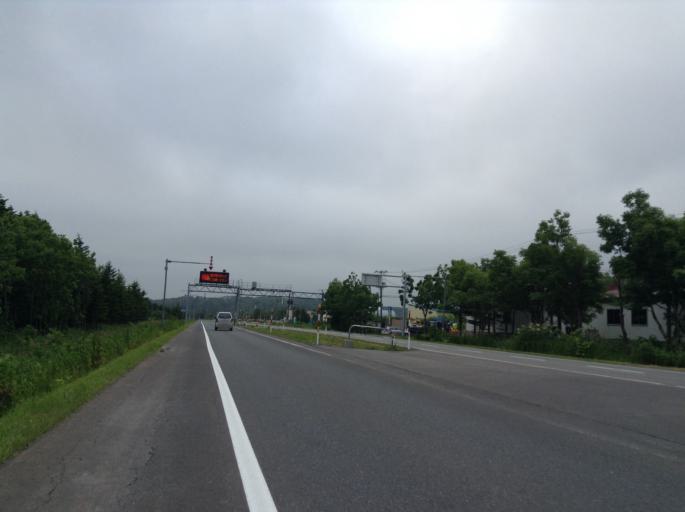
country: JP
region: Hokkaido
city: Wakkanai
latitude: 45.3656
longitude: 141.7286
